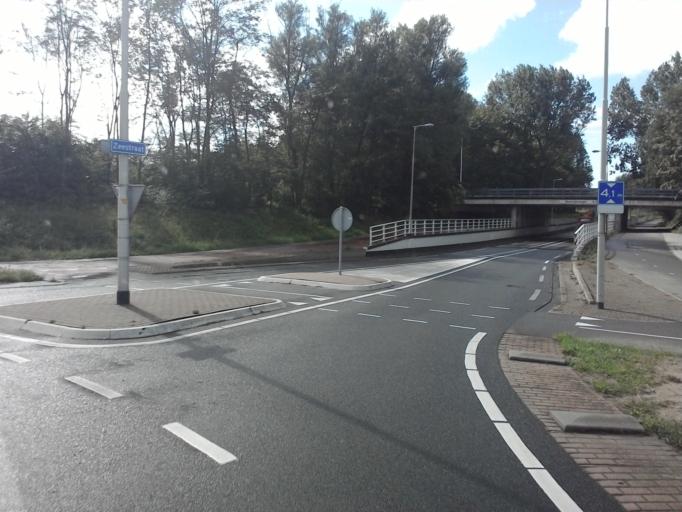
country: NL
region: North Holland
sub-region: Gemeente Beverwijk
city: Beverwijk
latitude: 52.4880
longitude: 4.6294
